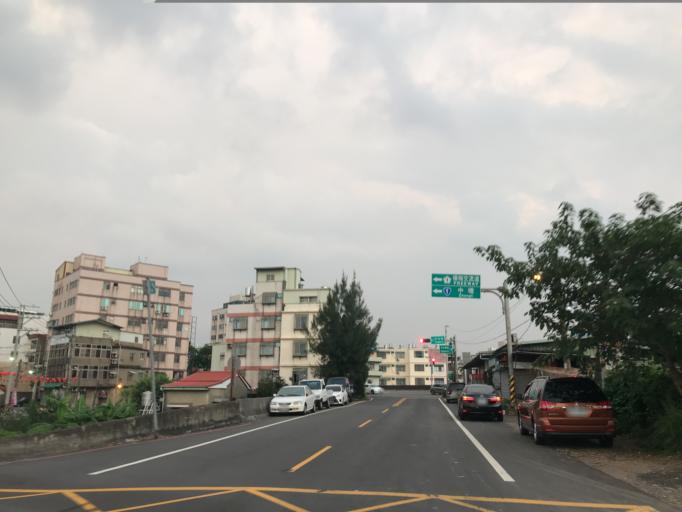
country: TW
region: Taiwan
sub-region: Hsinchu
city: Zhubei
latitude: 24.9067
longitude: 121.1409
